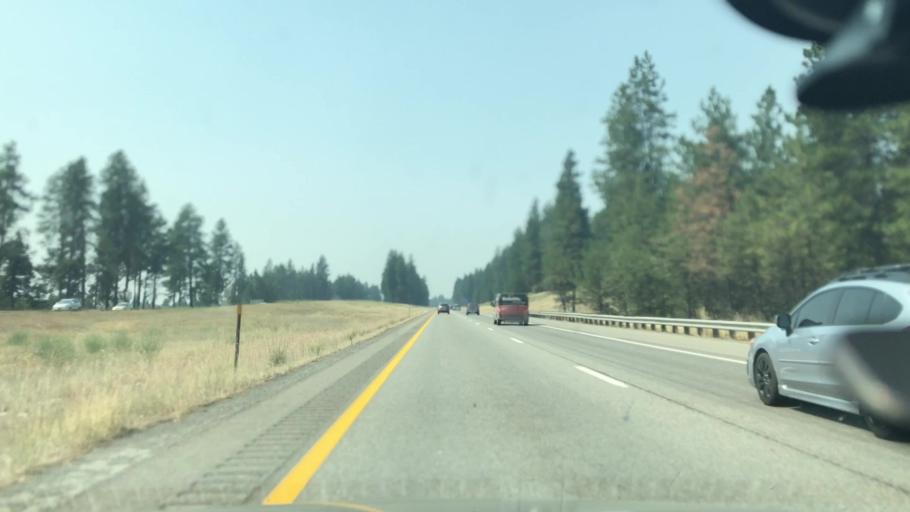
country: US
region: Idaho
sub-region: Kootenai County
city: Coeur d'Alene
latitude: 47.7046
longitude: -116.8351
